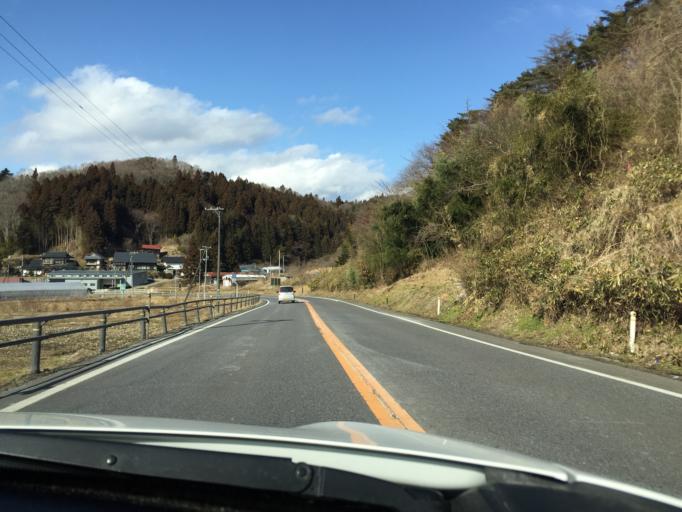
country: JP
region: Fukushima
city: Miharu
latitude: 37.2888
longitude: 140.5428
